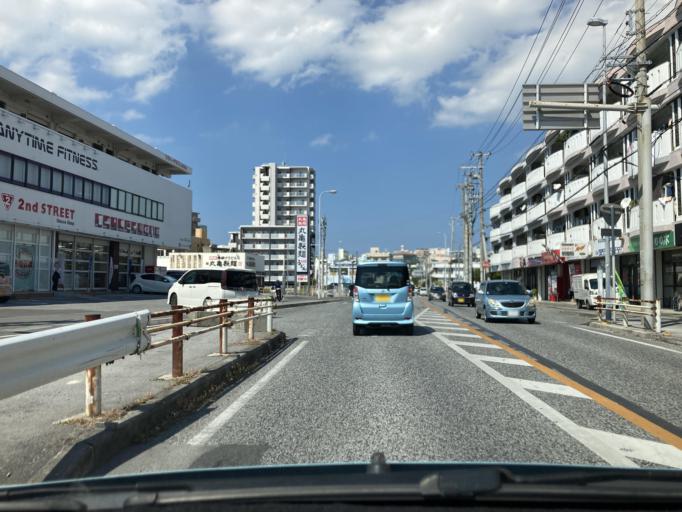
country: JP
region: Okinawa
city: Tomigusuku
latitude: 26.1915
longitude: 127.7076
